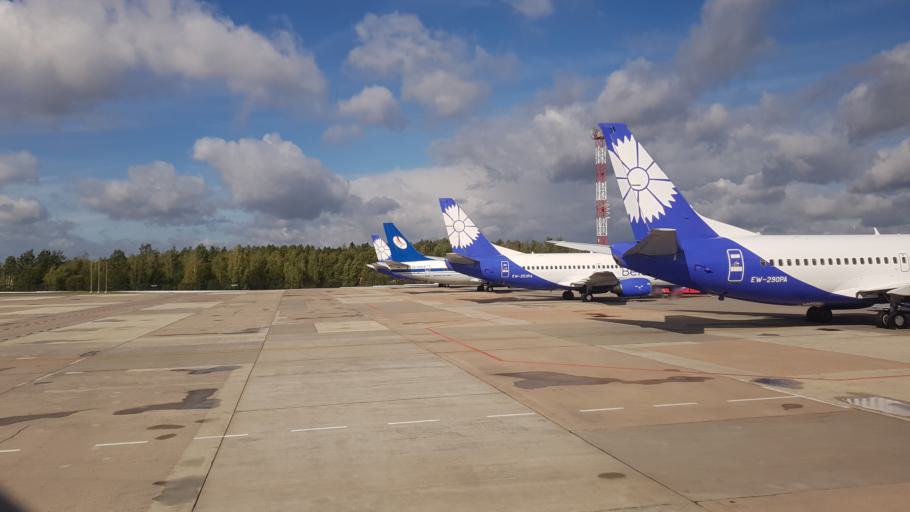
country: BY
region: Minsk
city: Smilavichy
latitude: 53.8903
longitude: 28.0286
